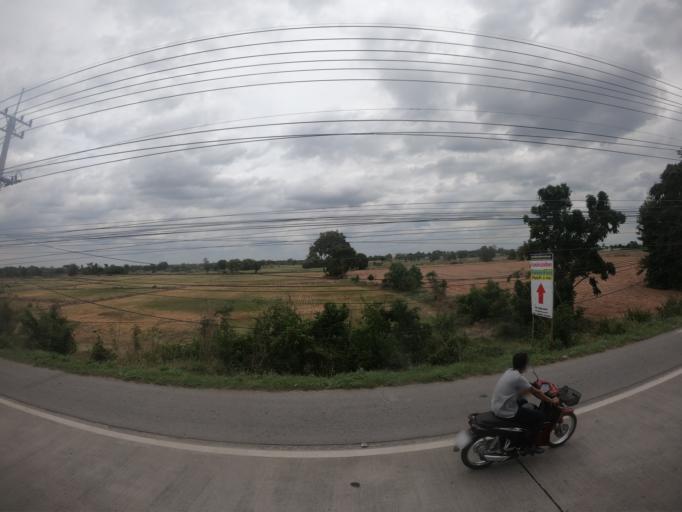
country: TH
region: Nakhon Ratchasima
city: Chok Chai
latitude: 14.8153
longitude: 102.1775
